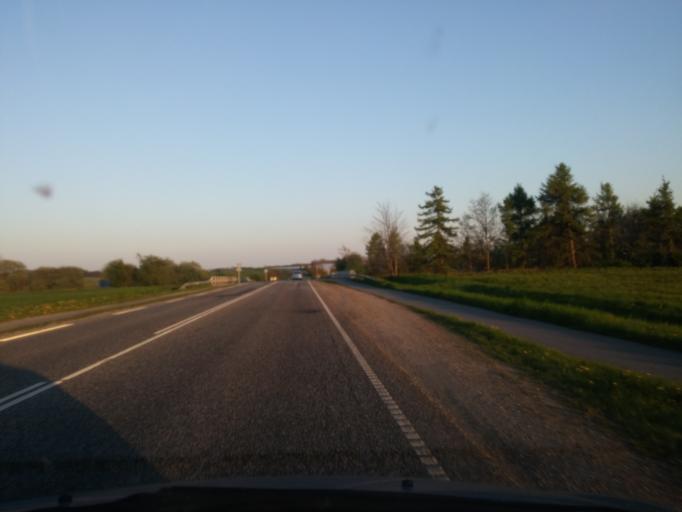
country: DK
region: South Denmark
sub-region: Nyborg Kommune
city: Nyborg
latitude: 55.3327
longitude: 10.7544
